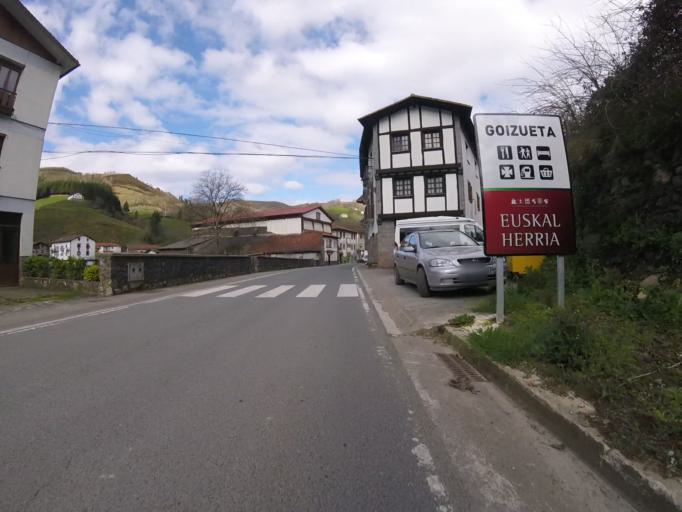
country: ES
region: Navarre
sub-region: Provincia de Navarra
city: Goizueta
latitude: 43.1702
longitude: -1.8630
